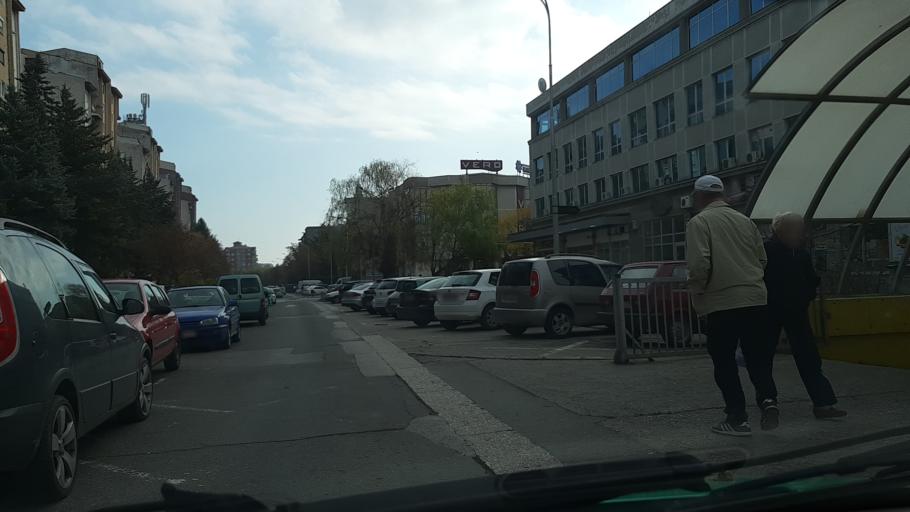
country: MK
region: Kisela Voda
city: Usje
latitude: 41.9853
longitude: 21.4680
